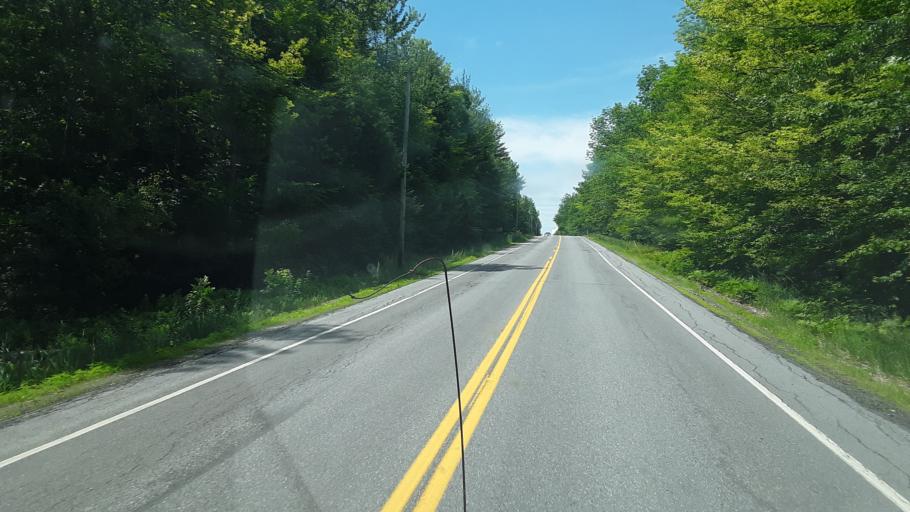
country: US
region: Maine
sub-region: Hancock County
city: Bucksport
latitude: 44.5687
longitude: -68.8280
